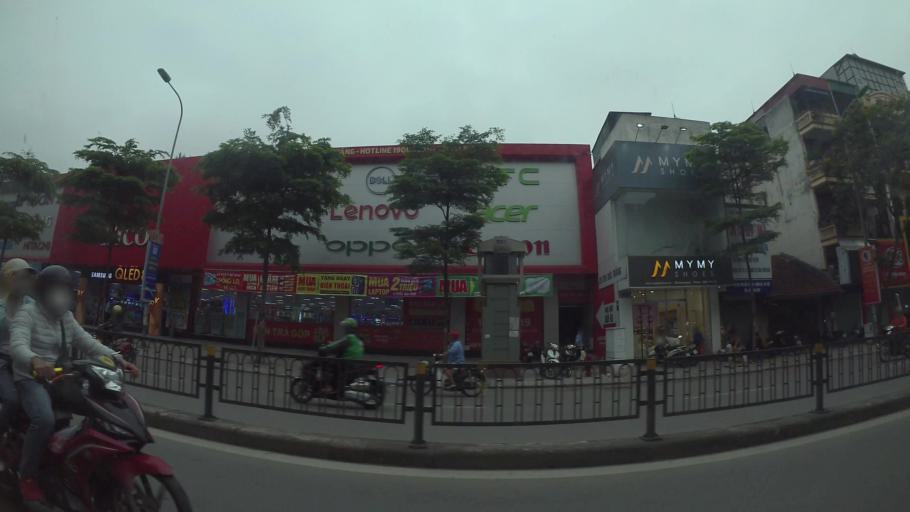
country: VN
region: Ha Noi
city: Dong Da
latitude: 21.0213
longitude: 105.8312
